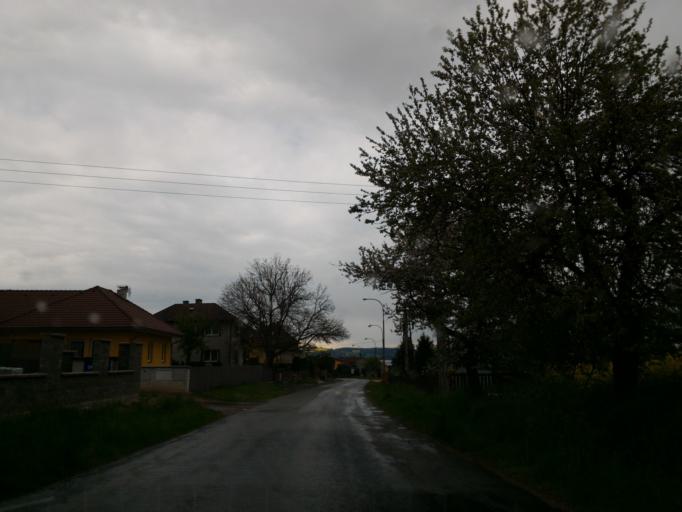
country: CZ
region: Vysocina
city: Ledec nad Sazavou
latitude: 49.6857
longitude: 15.2843
